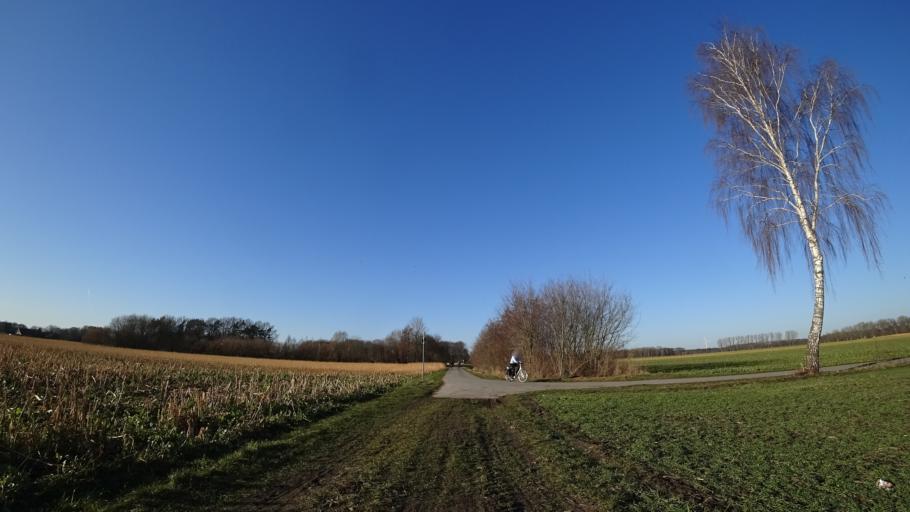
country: DE
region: North Rhine-Westphalia
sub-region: Regierungsbezirk Detmold
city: Guetersloh
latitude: 51.9354
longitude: 8.3248
